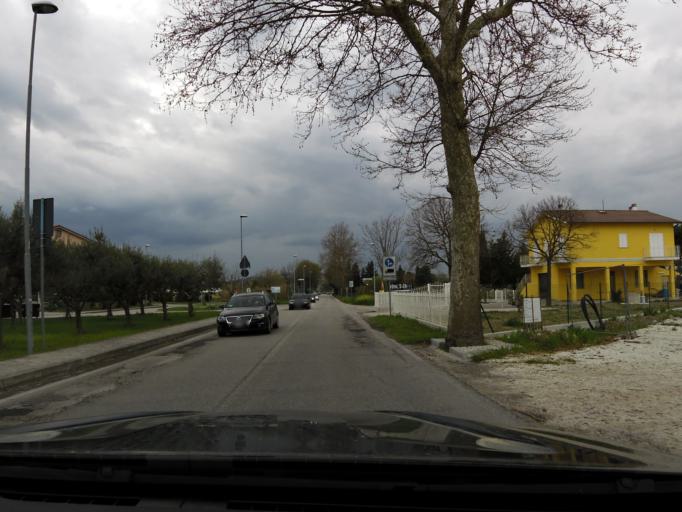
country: IT
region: The Marches
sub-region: Provincia di Ancona
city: Villa Musone
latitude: 43.4477
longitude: 13.6065
